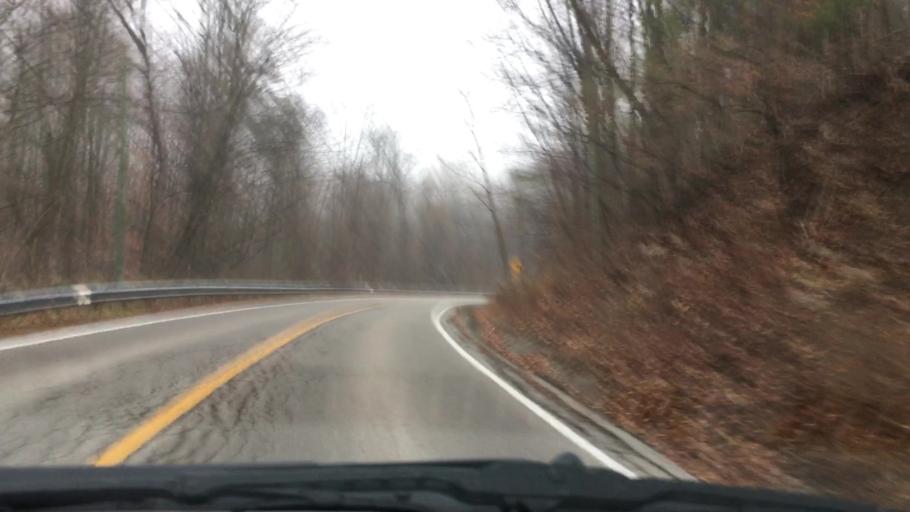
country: CA
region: Ontario
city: Hamilton
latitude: 43.3179
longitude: -79.8924
